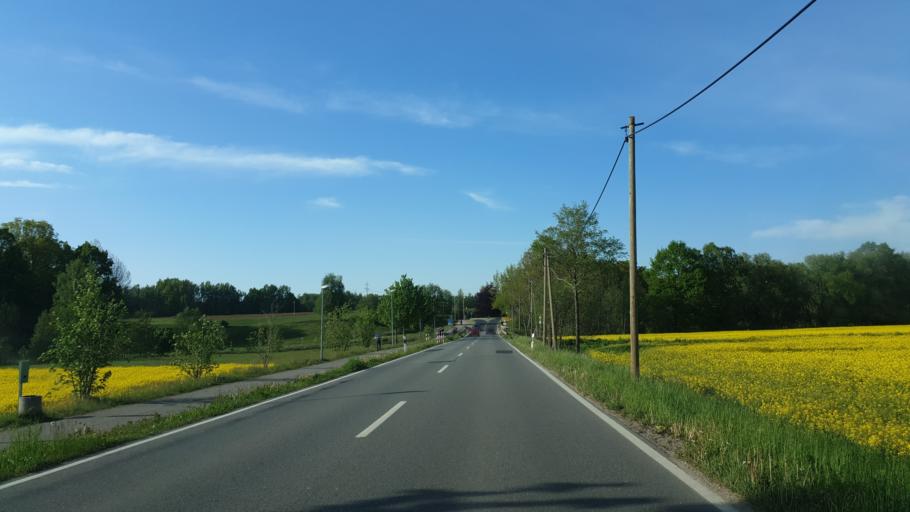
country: DE
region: Saxony
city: Neukirchen
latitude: 50.7680
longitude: 12.8756
